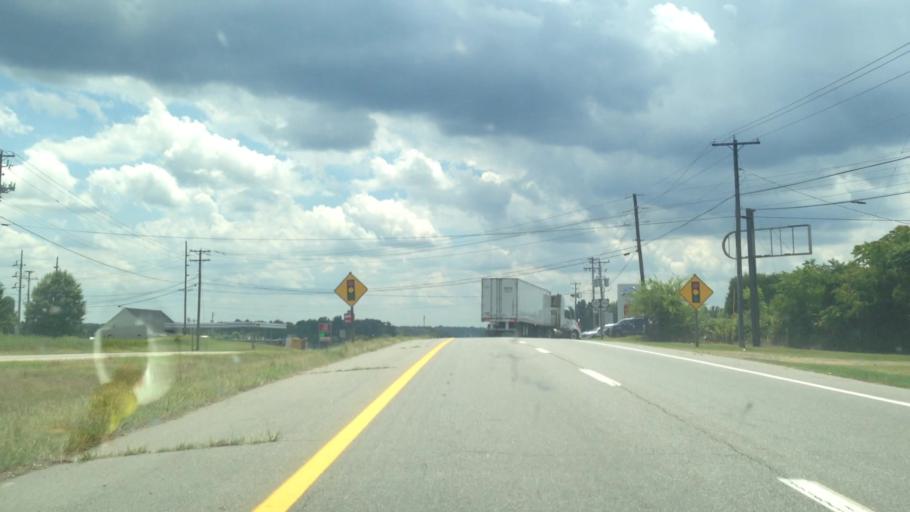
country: US
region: Virginia
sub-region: Henry County
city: Chatmoss
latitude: 36.6305
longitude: -79.8594
